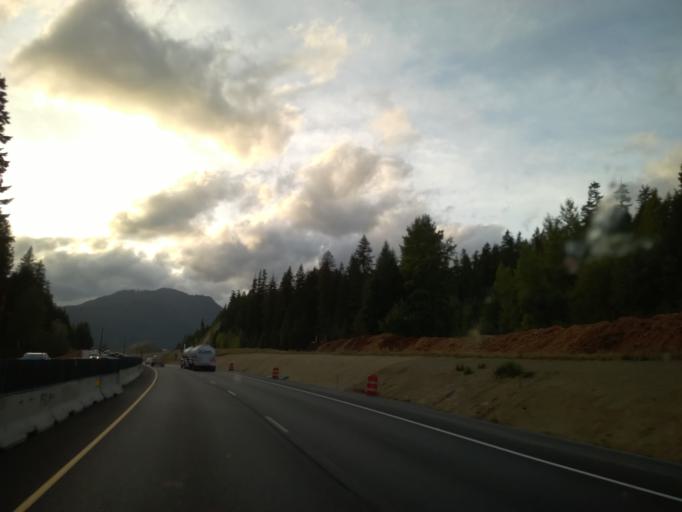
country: US
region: Washington
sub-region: Kittitas County
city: Cle Elum
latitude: 47.3266
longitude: -121.3315
